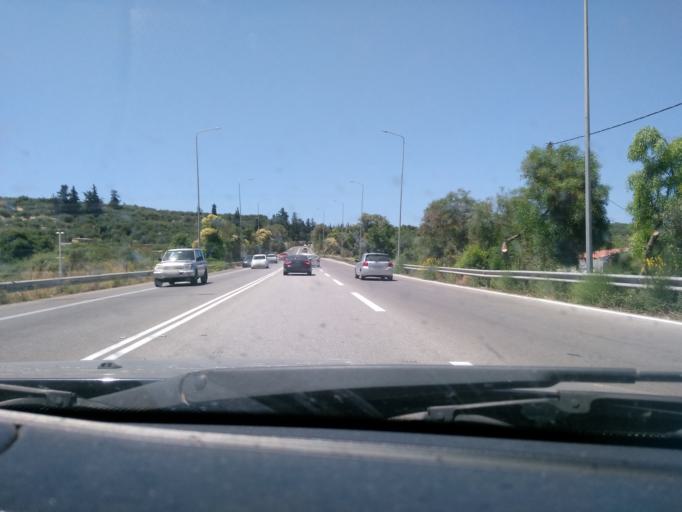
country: GR
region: Crete
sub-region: Nomos Chanias
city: Kalivai
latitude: 35.4458
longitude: 24.1684
